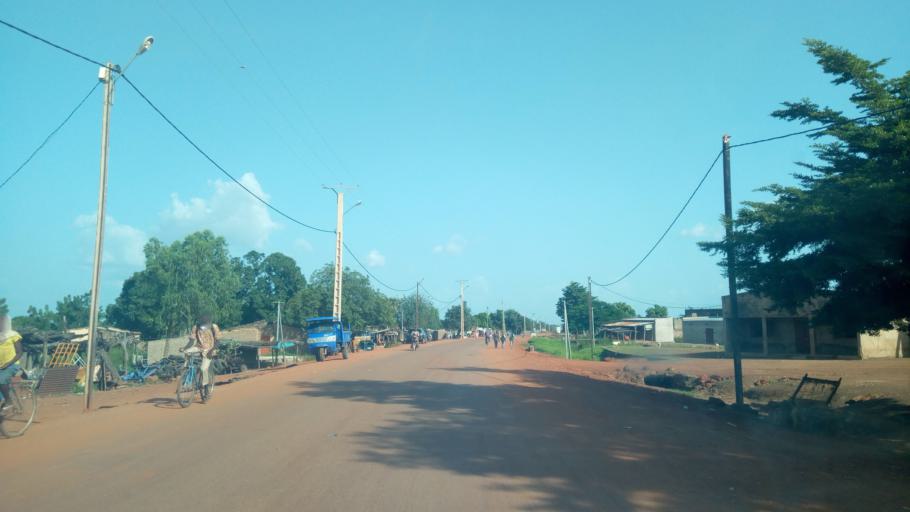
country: ML
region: Sikasso
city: Yorosso
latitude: 12.1820
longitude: -4.8021
